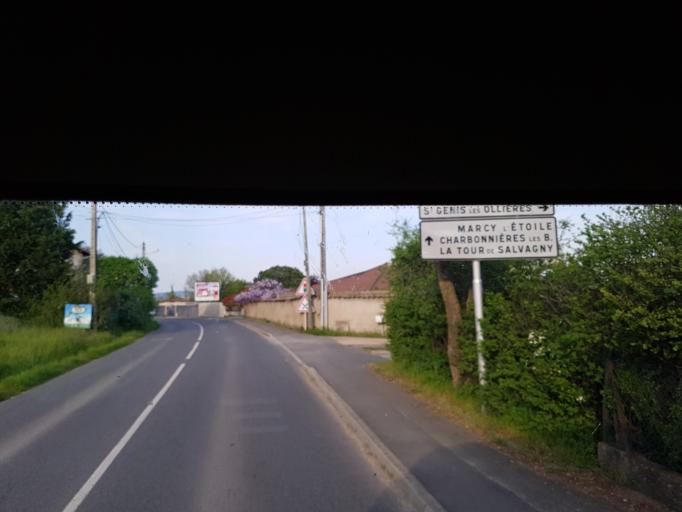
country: FR
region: Rhone-Alpes
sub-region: Departement du Rhone
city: Sainte-Consorce
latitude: 45.7647
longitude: 4.6971
